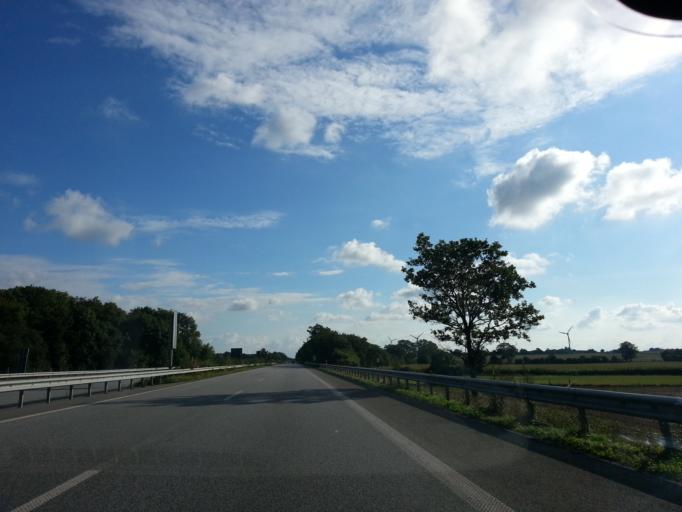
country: DE
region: Schleswig-Holstein
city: Kabelhorst
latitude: 54.2098
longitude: 10.9006
